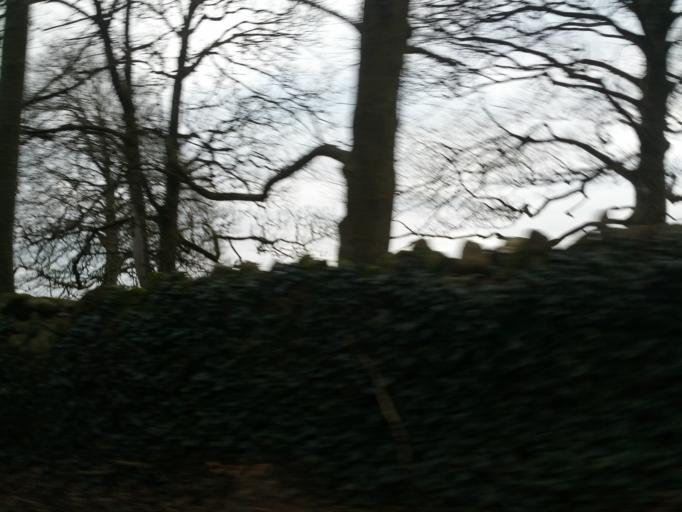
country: IE
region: Connaught
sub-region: County Galway
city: Oranmore
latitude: 53.1786
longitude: -8.8993
